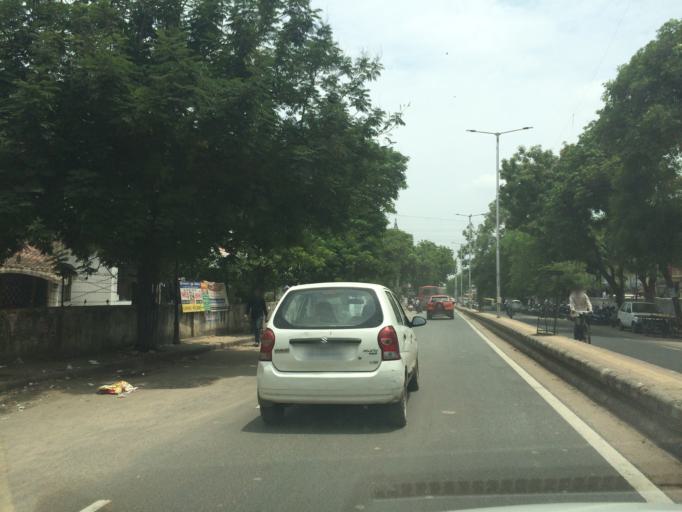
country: IN
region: Gujarat
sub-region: Ahmadabad
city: Ahmedabad
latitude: 23.0694
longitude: 72.5662
